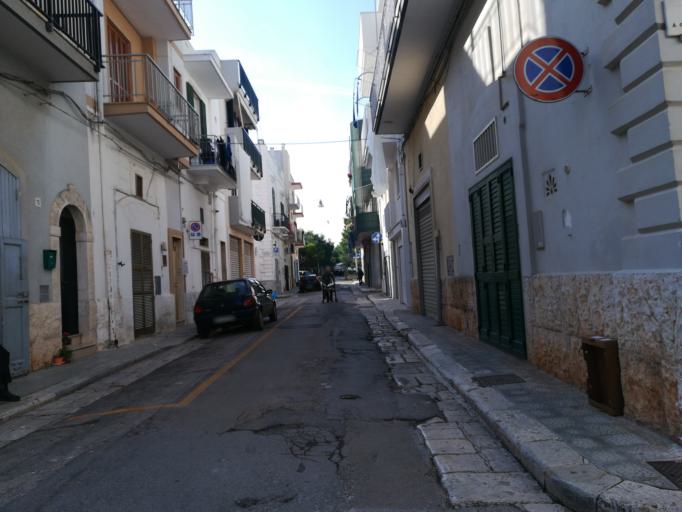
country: IT
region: Apulia
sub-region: Provincia di Bari
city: Polignano a Mare
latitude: 40.9931
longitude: 17.2222
